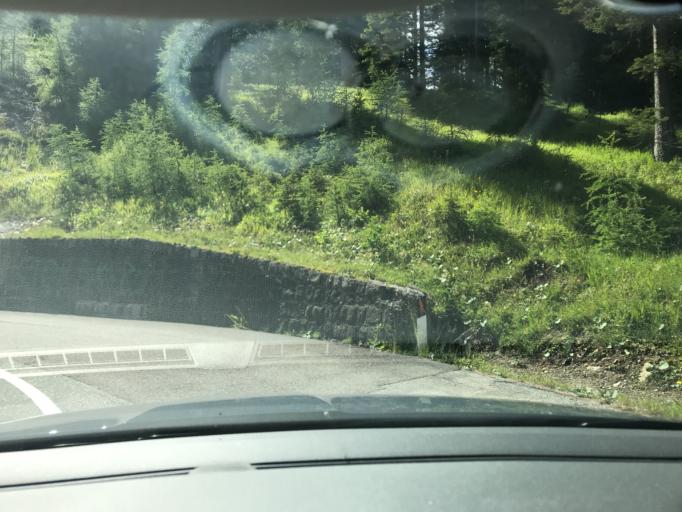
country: IT
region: Veneto
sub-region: Provincia di Belluno
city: Livinallongo del Col di Lana
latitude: 46.5518
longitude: 11.9767
